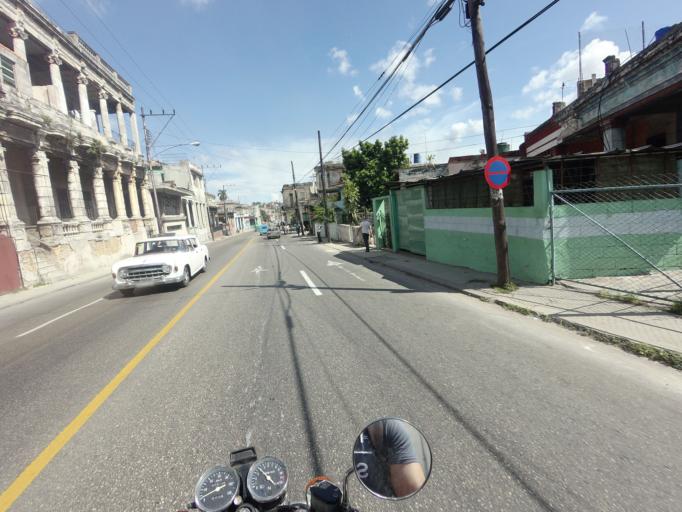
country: CU
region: La Habana
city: Diez de Octubre
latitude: 23.0920
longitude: -82.3644
